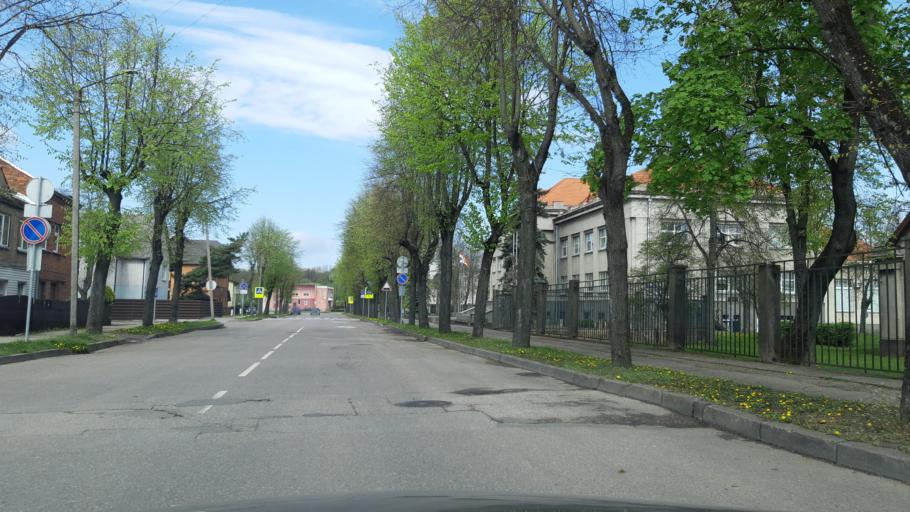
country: LT
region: Kauno apskritis
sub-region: Kaunas
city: Kaunas
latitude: 54.9074
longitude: 23.8802
